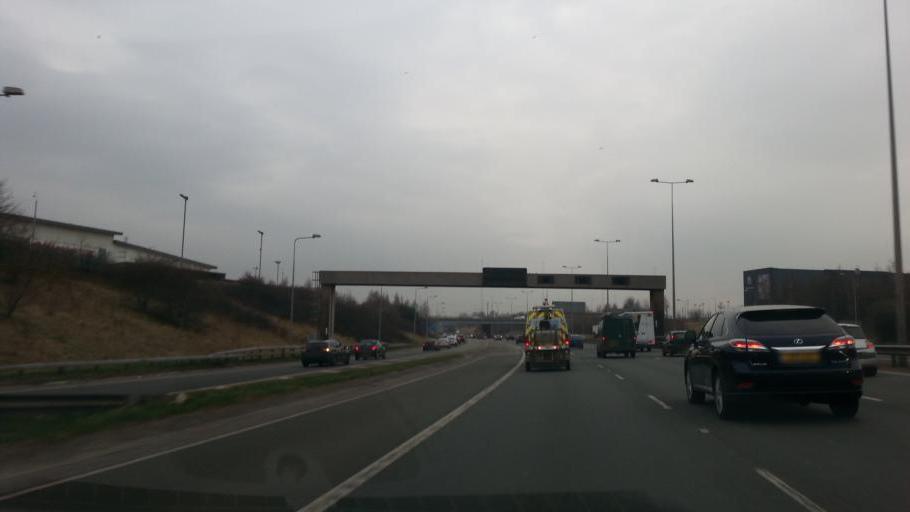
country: GB
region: England
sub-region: Borough of Tameside
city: Ashton-under-Lyne
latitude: 53.4839
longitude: -2.1154
